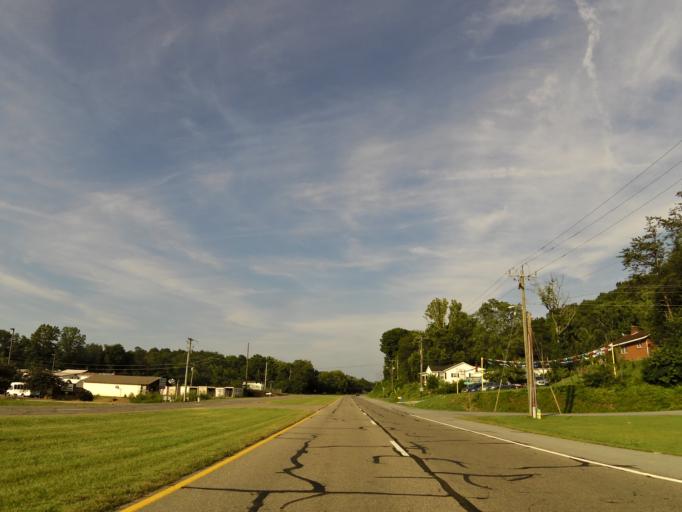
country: US
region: Tennessee
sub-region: Sevier County
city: Sevierville
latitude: 35.8711
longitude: -83.5955
